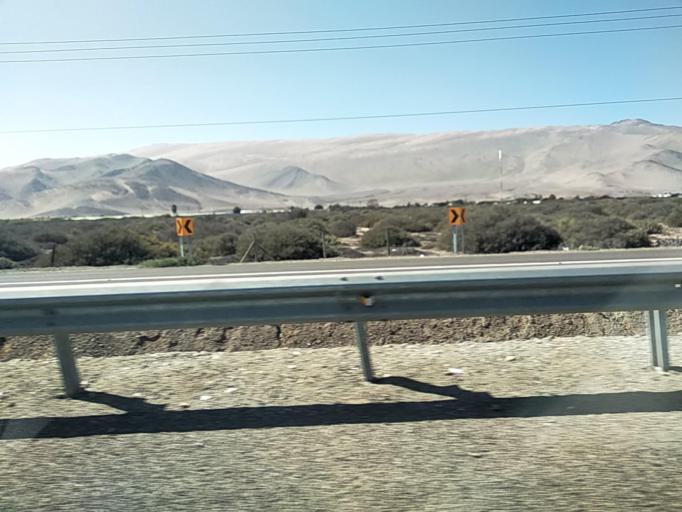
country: CL
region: Atacama
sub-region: Provincia de Copiapo
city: Copiapo
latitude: -27.2943
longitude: -70.4683
